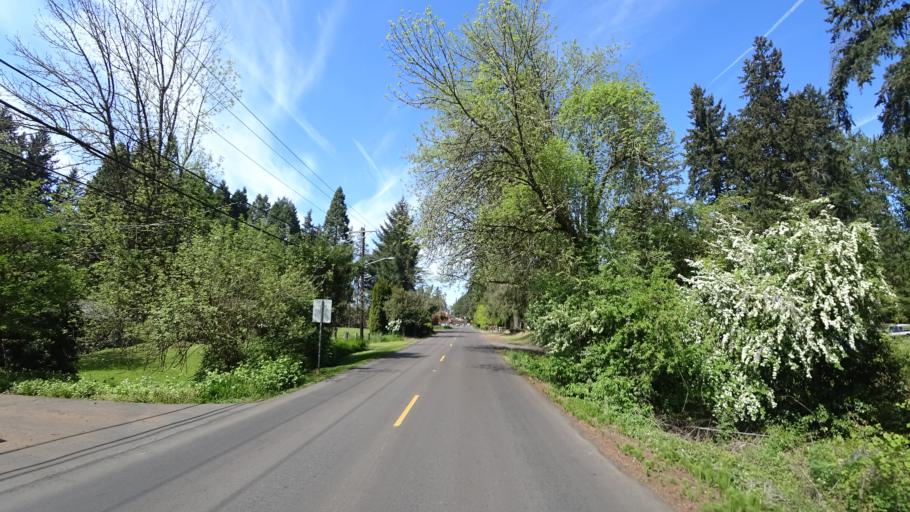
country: US
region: Oregon
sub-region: Washington County
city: Hillsboro
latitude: 45.5184
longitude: -122.9581
